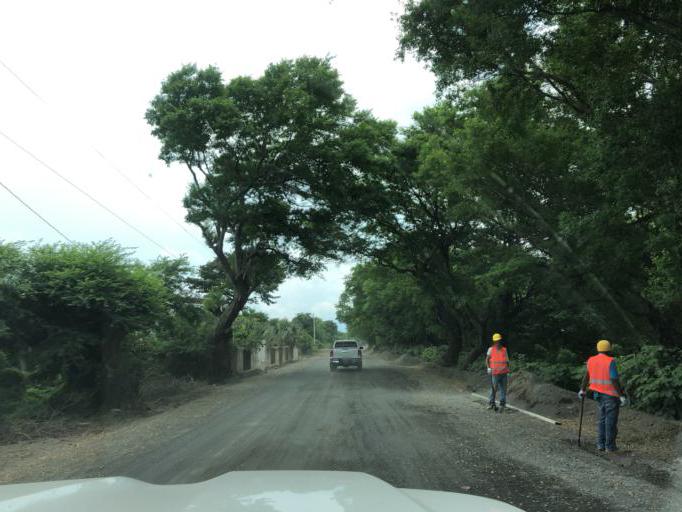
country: NI
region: Granada
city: Granada
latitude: 12.0104
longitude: -85.9323
